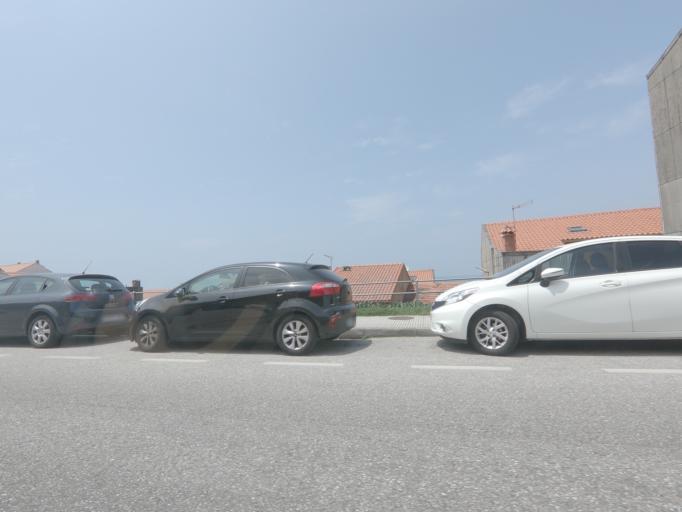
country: ES
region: Galicia
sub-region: Provincia de Pontevedra
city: A Guarda
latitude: 41.8982
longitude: -8.8732
